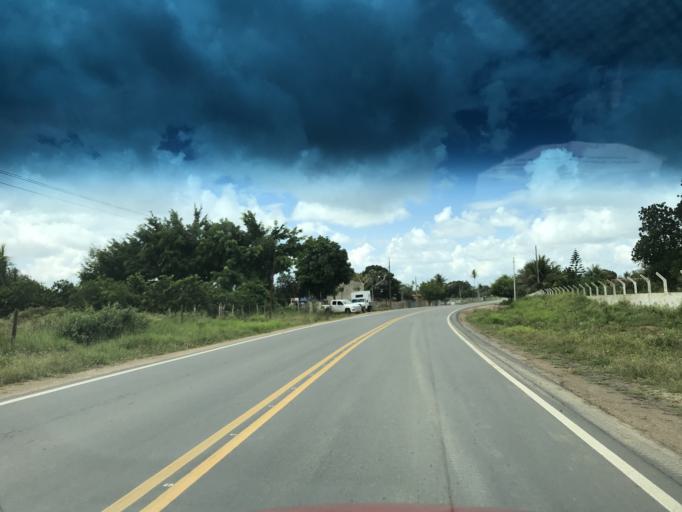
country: BR
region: Bahia
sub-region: Conceicao Do Almeida
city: Conceicao do Almeida
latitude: -12.7257
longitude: -39.2042
